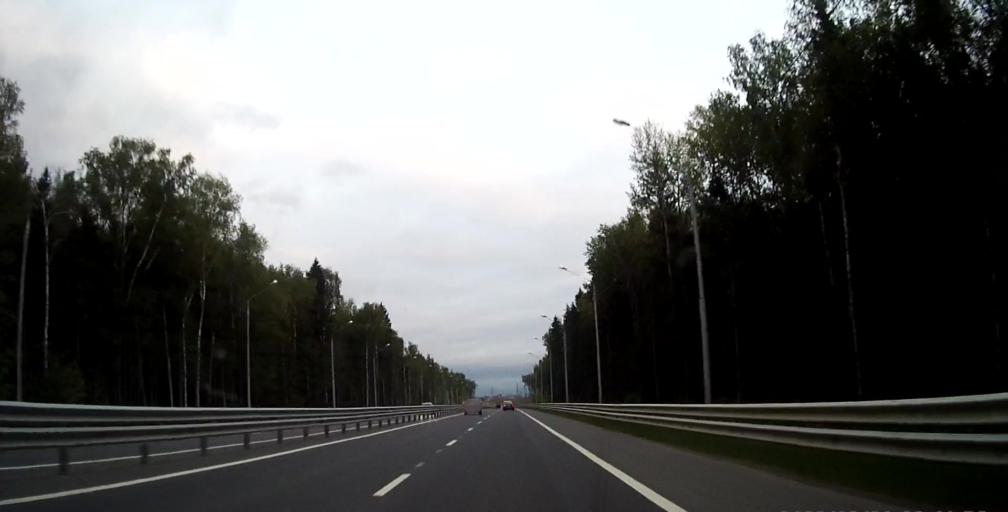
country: RU
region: Moskovskaya
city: Klimovsk
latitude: 55.3941
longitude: 37.5036
